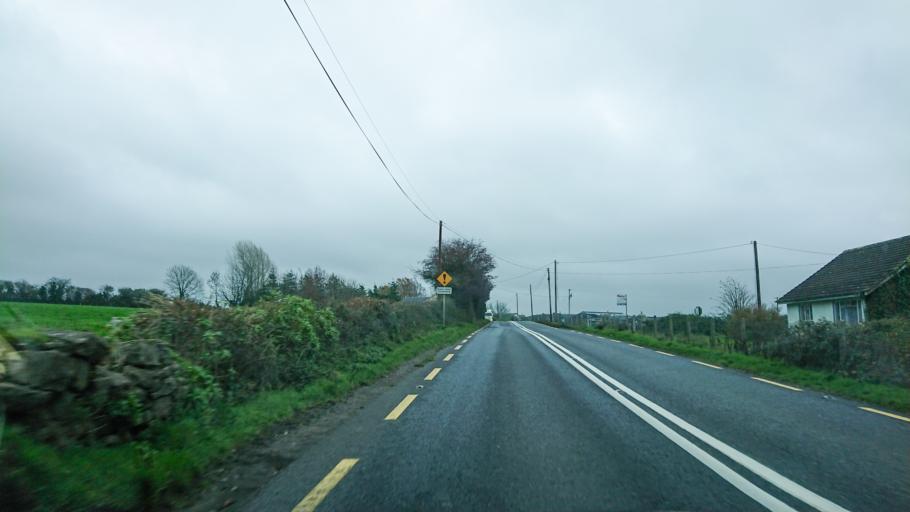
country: IE
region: Leinster
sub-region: Kilkenny
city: Mooncoin
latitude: 52.3050
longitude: -7.2785
